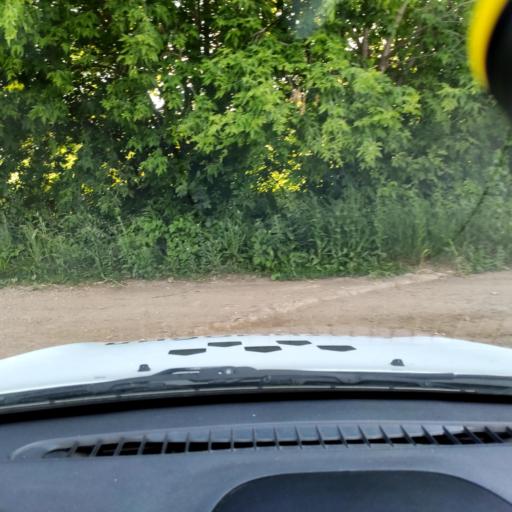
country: RU
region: Samara
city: Zhigulevsk
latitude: 53.3984
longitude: 49.5471
